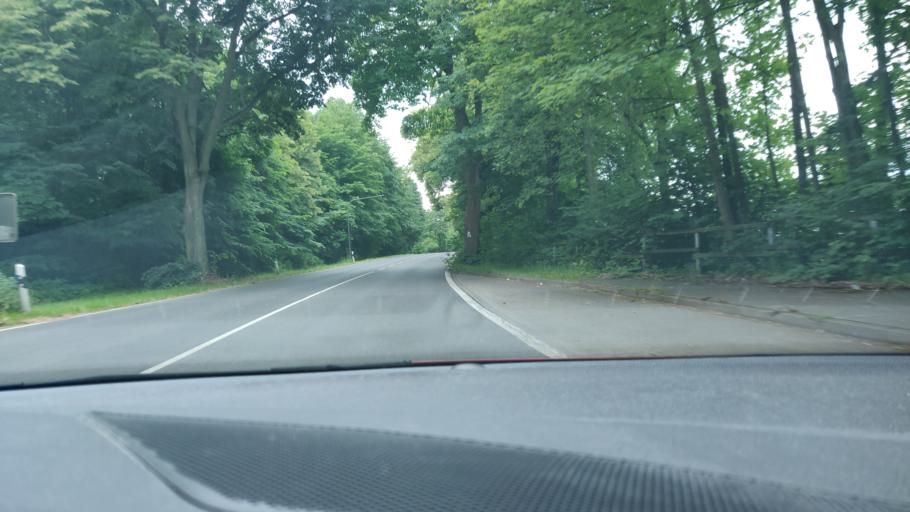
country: DE
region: North Rhine-Westphalia
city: Haan
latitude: 51.2191
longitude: 7.0486
